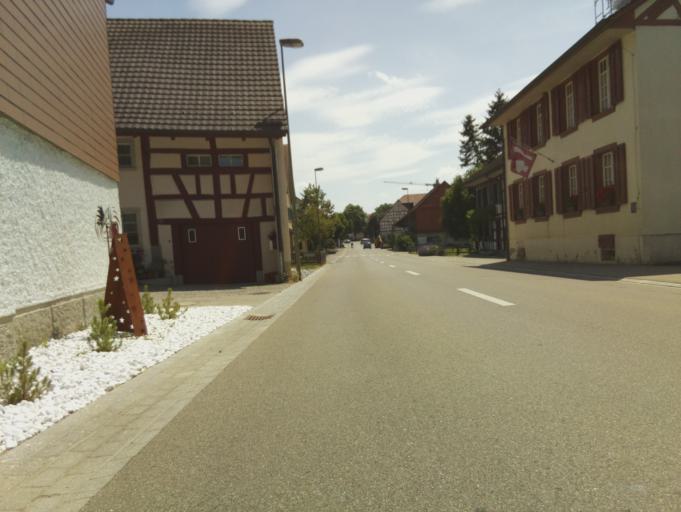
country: CH
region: Zurich
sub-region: Bezirk Andelfingen
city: Marthalen
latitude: 47.6243
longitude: 8.6756
